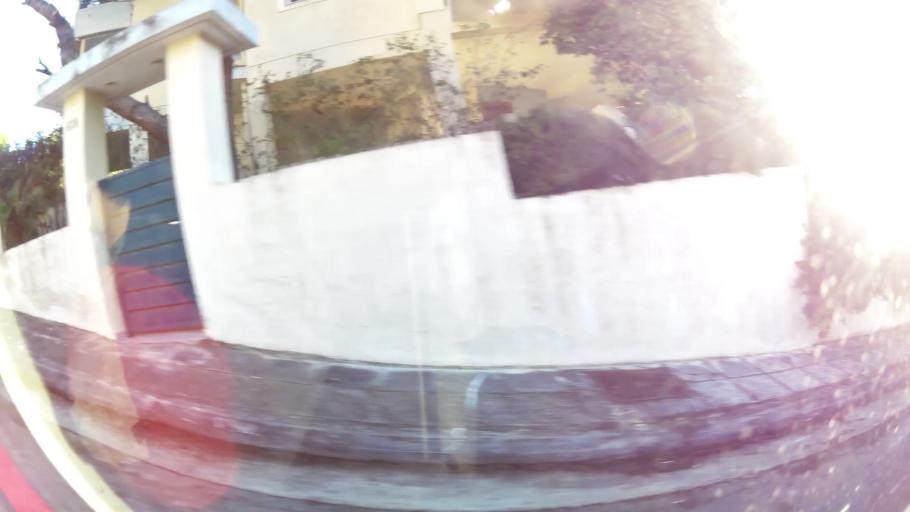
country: GR
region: Attica
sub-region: Nomarchia Anatolikis Attikis
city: Rafina
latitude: 38.0209
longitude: 24.0023
